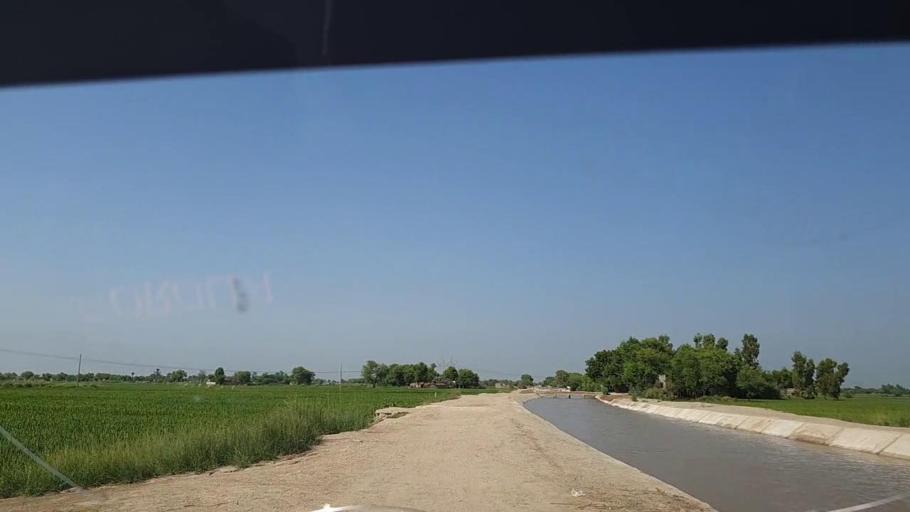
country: PK
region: Sindh
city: Ghauspur
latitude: 28.1632
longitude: 69.0951
